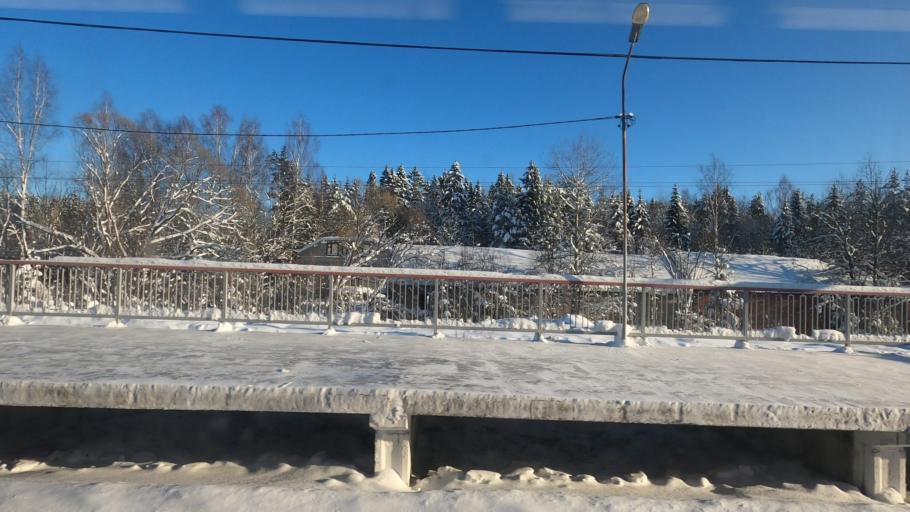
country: RU
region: Moskovskaya
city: Verbilki
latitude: 56.5349
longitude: 37.5602
